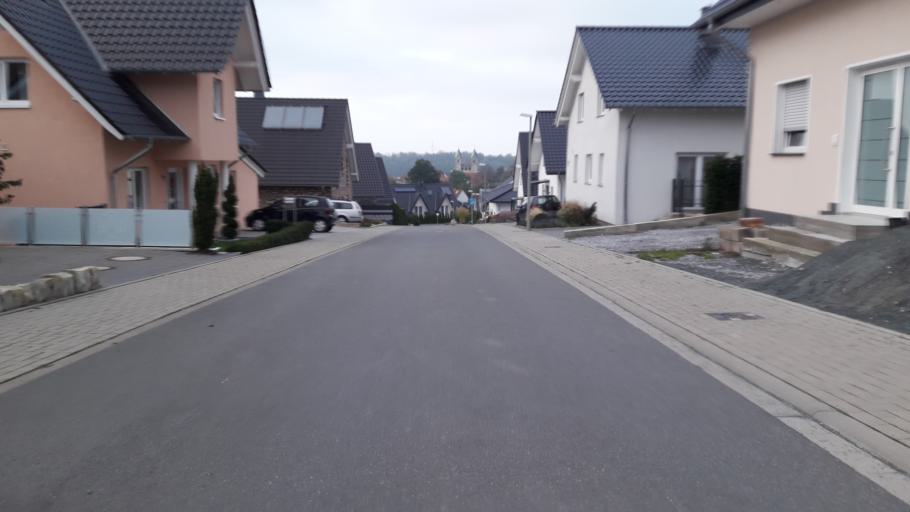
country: DE
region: North Rhine-Westphalia
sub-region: Regierungsbezirk Detmold
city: Paderborn
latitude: 51.6638
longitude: 8.7231
